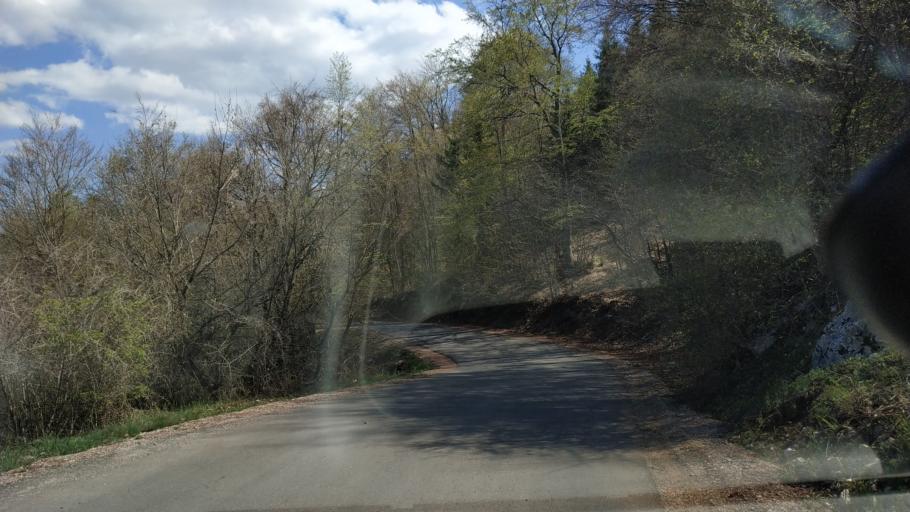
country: RS
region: Central Serbia
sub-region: Zajecarski Okrug
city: Soko Banja
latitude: 43.5852
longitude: 21.8889
